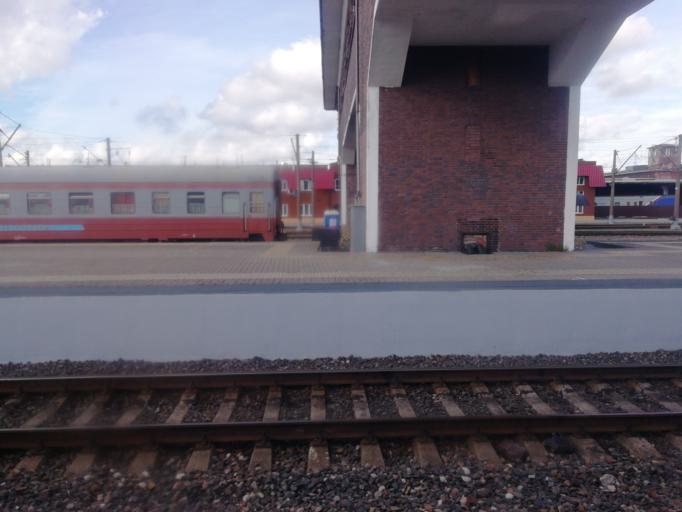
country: RU
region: Kaliningrad
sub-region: Gorod Kaliningrad
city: Kaliningrad
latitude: 54.6946
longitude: 20.4951
